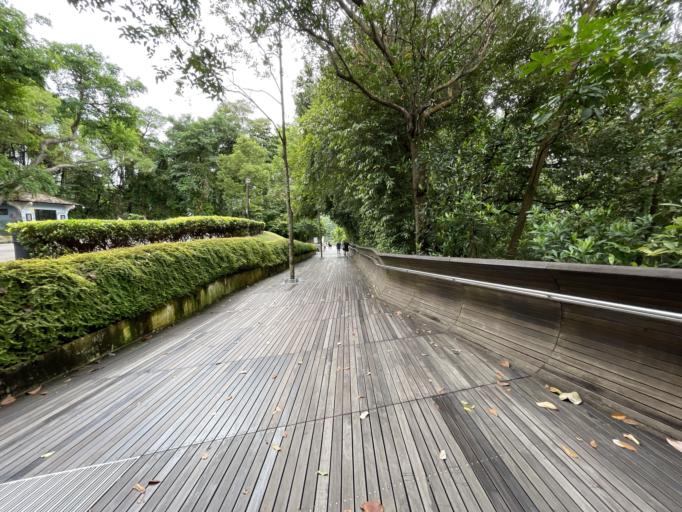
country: SG
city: Singapore
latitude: 1.2770
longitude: 103.8143
